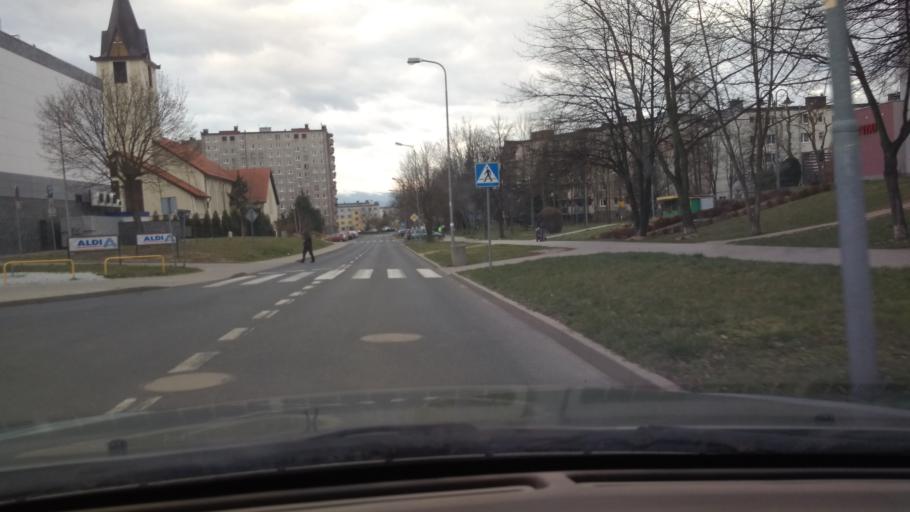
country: PL
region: Lower Silesian Voivodeship
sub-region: Powiat jeleniogorski
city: Jezow Sudecki
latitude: 50.9191
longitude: 15.7542
